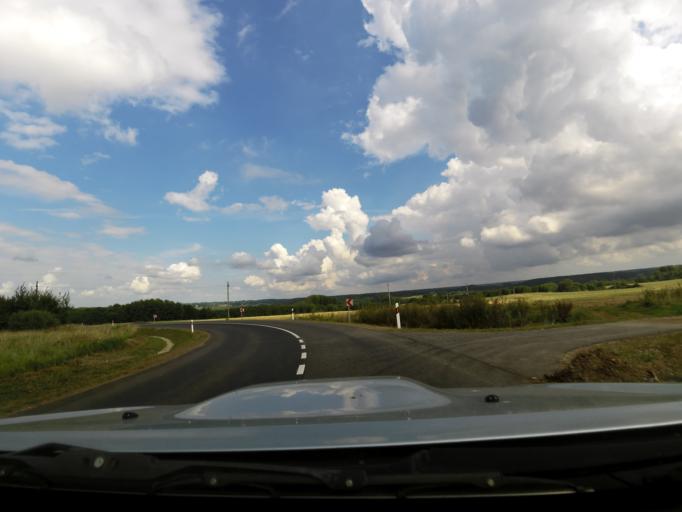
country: LT
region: Vilnius County
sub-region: Vilniaus Rajonas
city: Vievis
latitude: 54.8536
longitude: 24.8359
